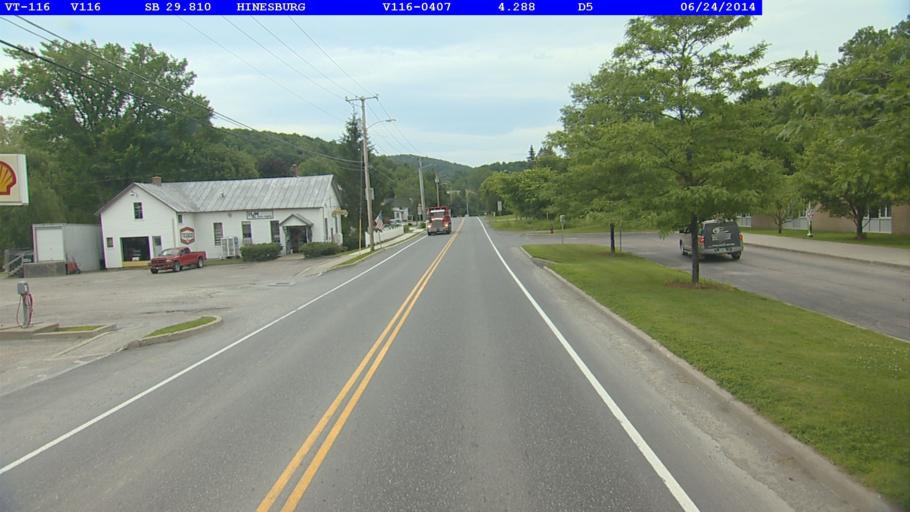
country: US
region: Vermont
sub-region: Chittenden County
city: Hinesburg
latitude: 44.3267
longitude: -73.1079
